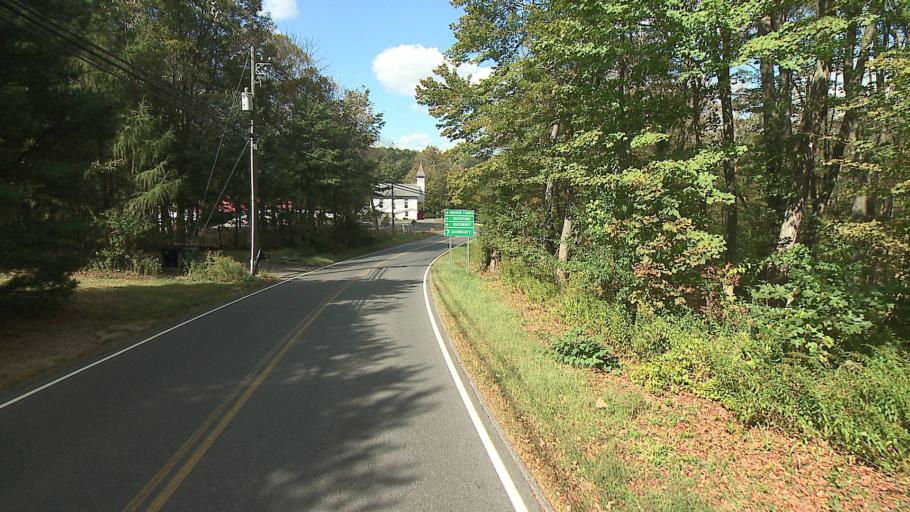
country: US
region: Connecticut
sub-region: New Haven County
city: Seymour
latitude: 41.3770
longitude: -73.1257
